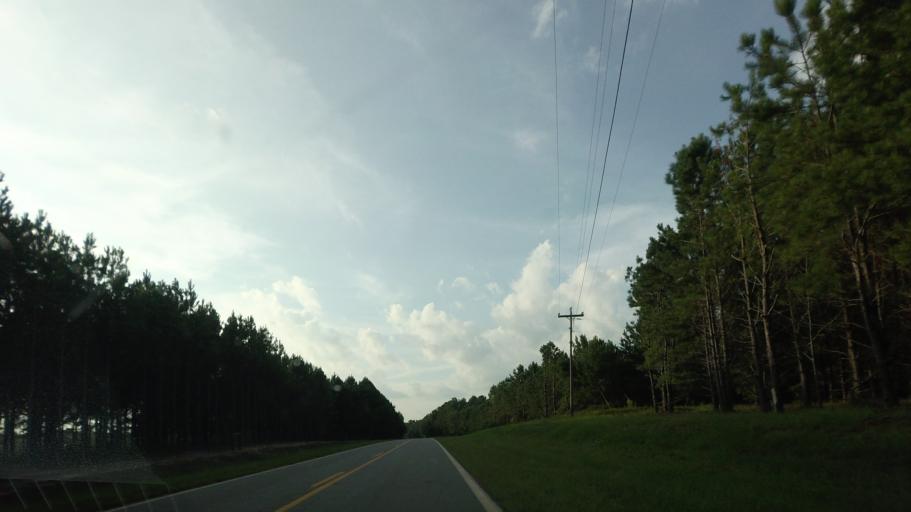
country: US
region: Georgia
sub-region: Wilkinson County
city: Gordon
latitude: 32.8194
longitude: -83.4022
